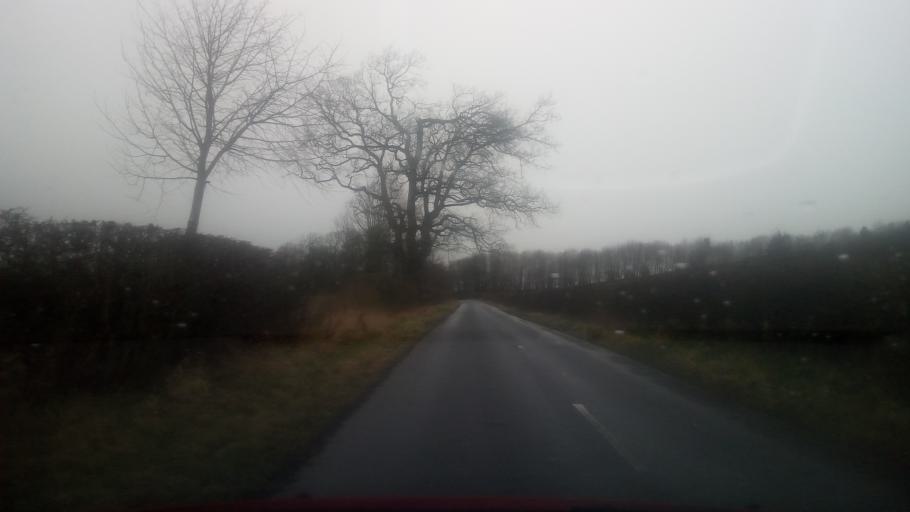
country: GB
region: Scotland
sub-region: The Scottish Borders
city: Earlston
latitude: 55.6276
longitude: -2.6707
